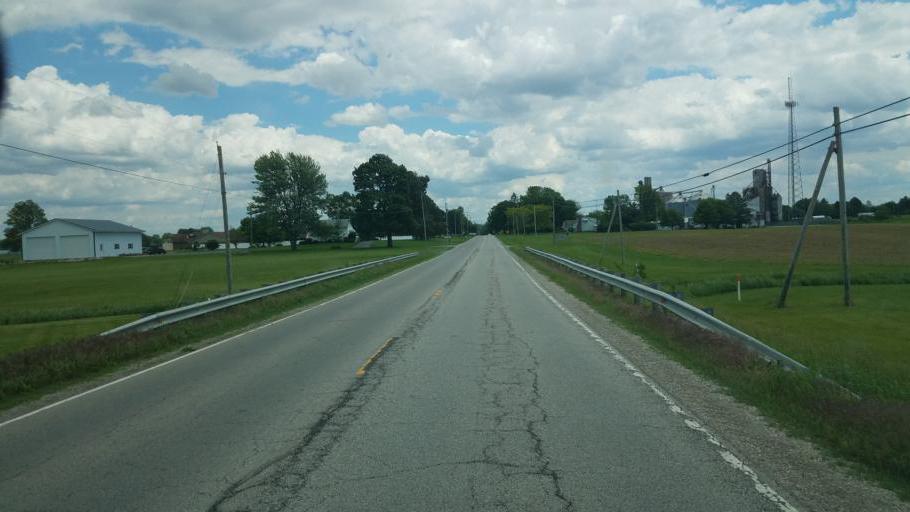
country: US
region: Ohio
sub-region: Crawford County
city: Bucyrus
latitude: 40.8131
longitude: -82.9960
